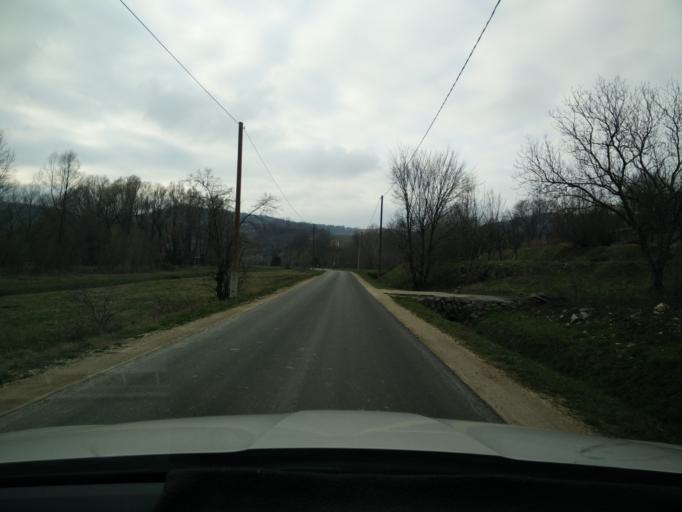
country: HU
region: Tolna
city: Szekszard
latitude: 46.3344
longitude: 18.6647
